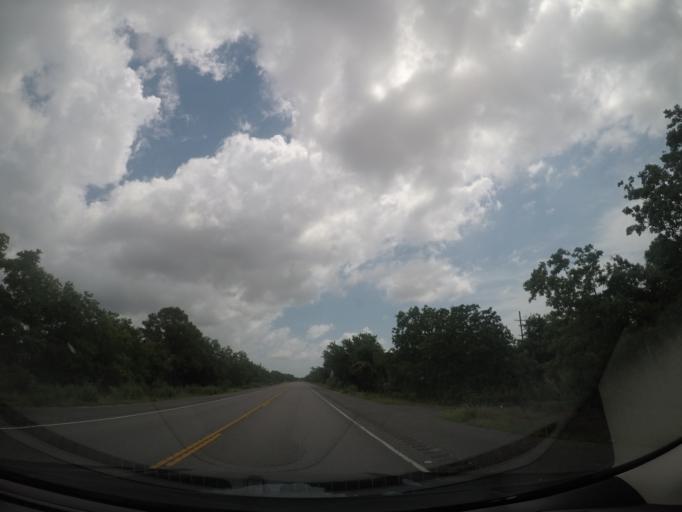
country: US
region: Louisiana
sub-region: Saint Tammany Parish
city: Eden Isle
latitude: 30.0841
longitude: -89.7899
